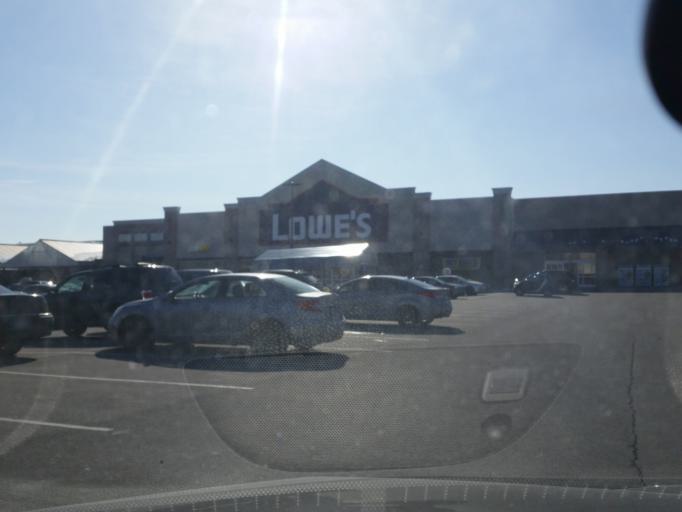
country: CA
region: Ontario
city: Ottawa
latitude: 45.3380
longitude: -75.7151
